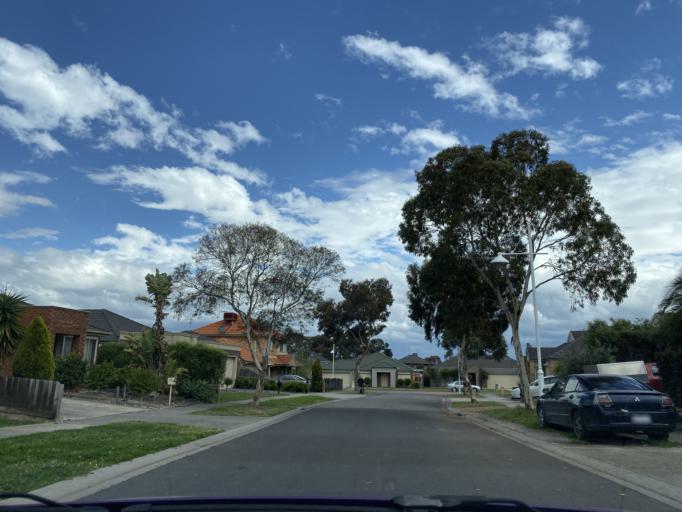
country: AU
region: Victoria
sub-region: Whittlesea
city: Mernda
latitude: -37.6266
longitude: 145.0690
